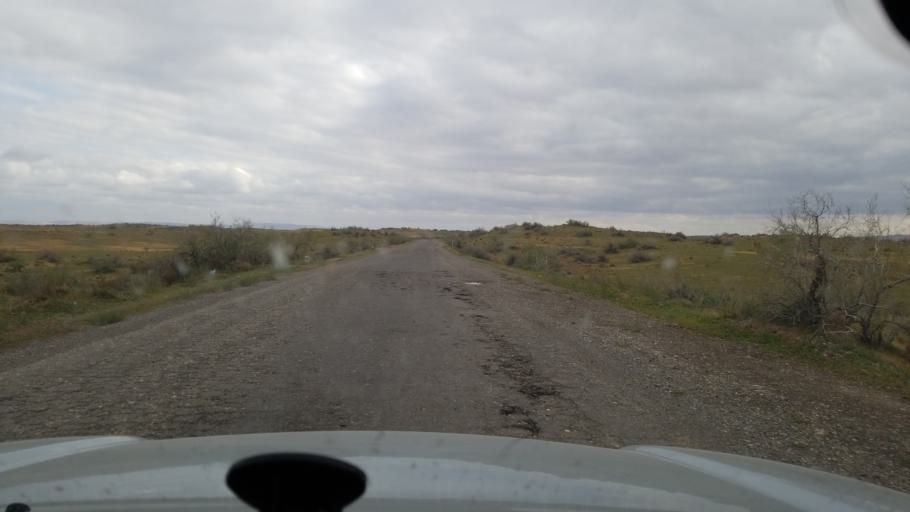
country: TM
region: Mary
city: Serhetabat
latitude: 36.0501
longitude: 62.6168
